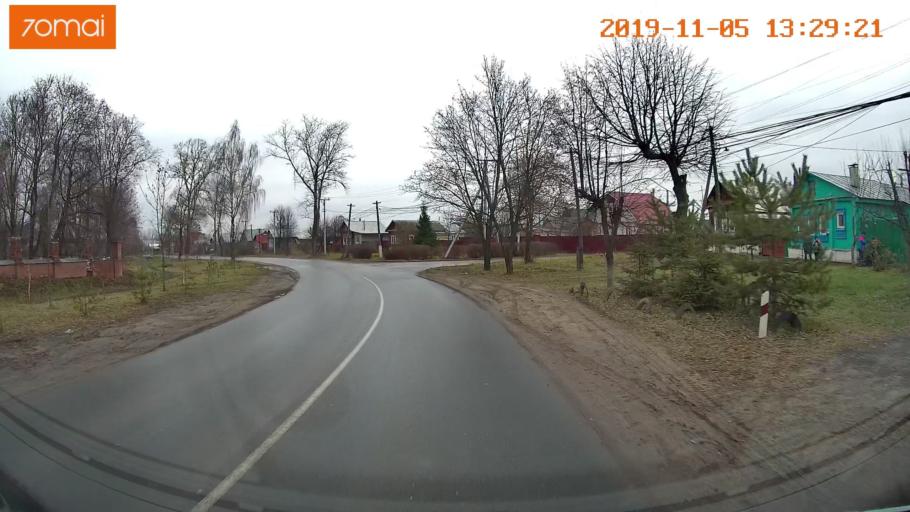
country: RU
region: Ivanovo
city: Shuya
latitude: 56.8600
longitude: 41.3972
